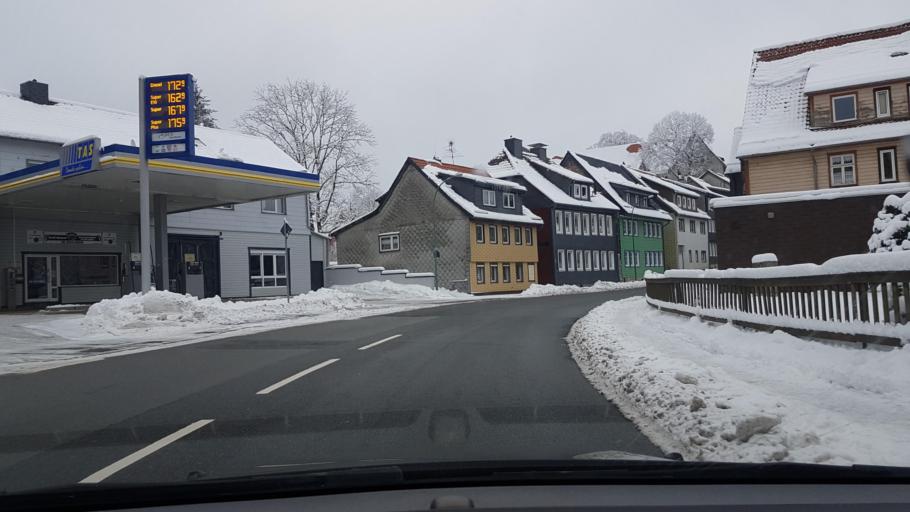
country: DE
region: Lower Saxony
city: Clausthal-Zellerfeld
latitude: 51.8045
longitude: 10.3299
